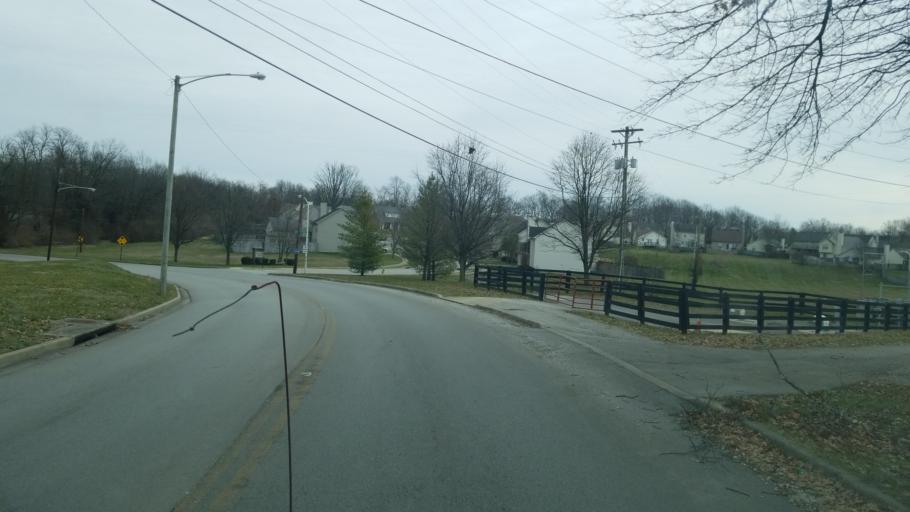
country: US
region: Kentucky
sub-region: Fayette County
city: Lexington-Fayette
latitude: 38.0771
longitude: -84.4522
